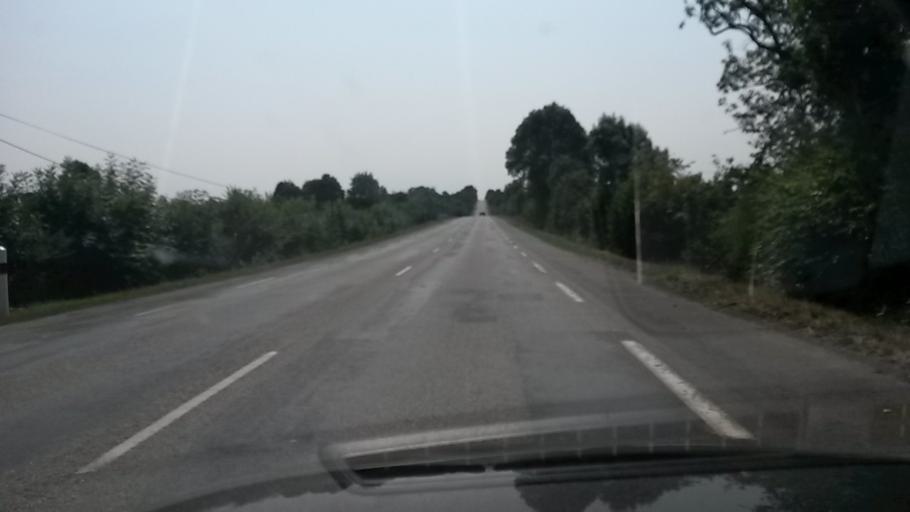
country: FR
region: Pays de la Loire
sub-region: Departement de la Mayenne
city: Chateau-Gontier
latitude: 47.8834
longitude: -0.6831
